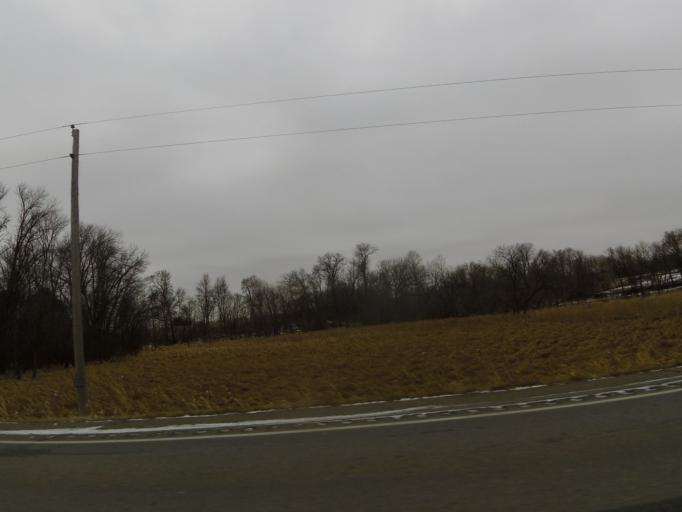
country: US
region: Minnesota
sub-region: Hennepin County
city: Independence
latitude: 45.0160
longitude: -93.6971
